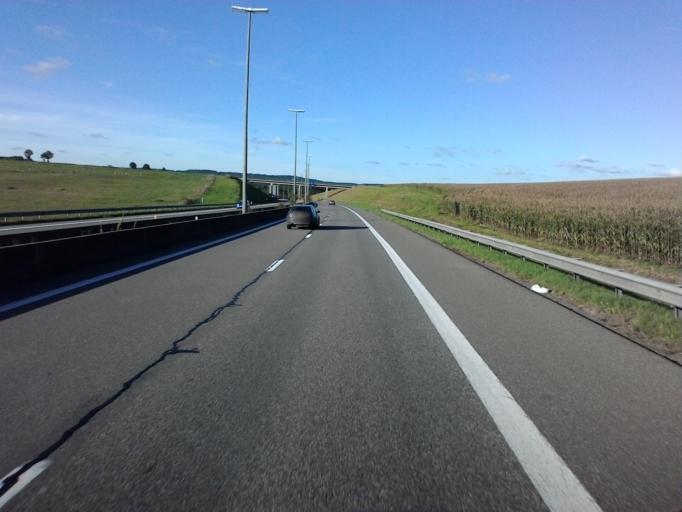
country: BE
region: Wallonia
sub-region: Province du Luxembourg
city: Houffalize
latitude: 50.1554
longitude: 5.7936
